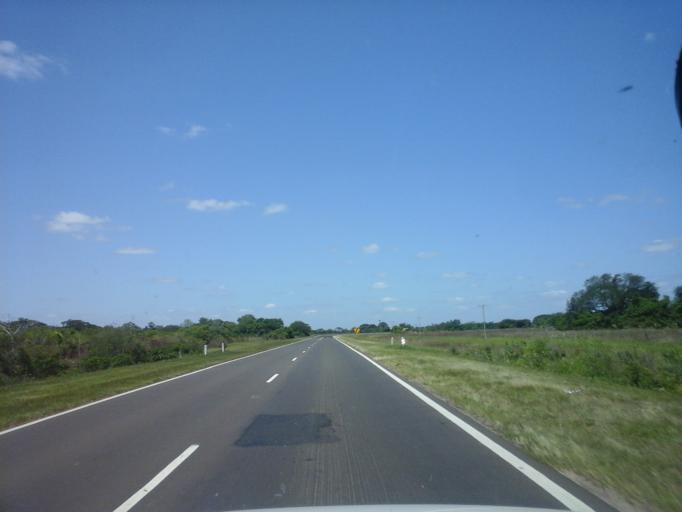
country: AR
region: Corrientes
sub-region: Departamento de Itati
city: Itati
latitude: -27.3381
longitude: -58.1792
